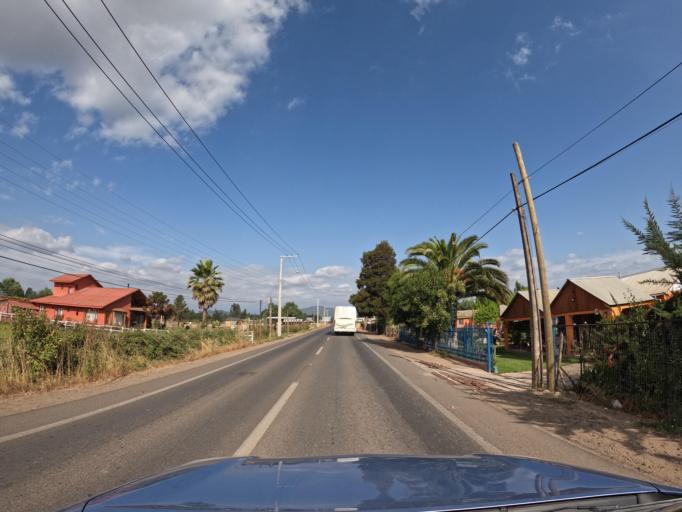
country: CL
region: Maule
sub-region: Provincia de Curico
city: Molina
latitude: -35.2753
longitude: -71.2911
